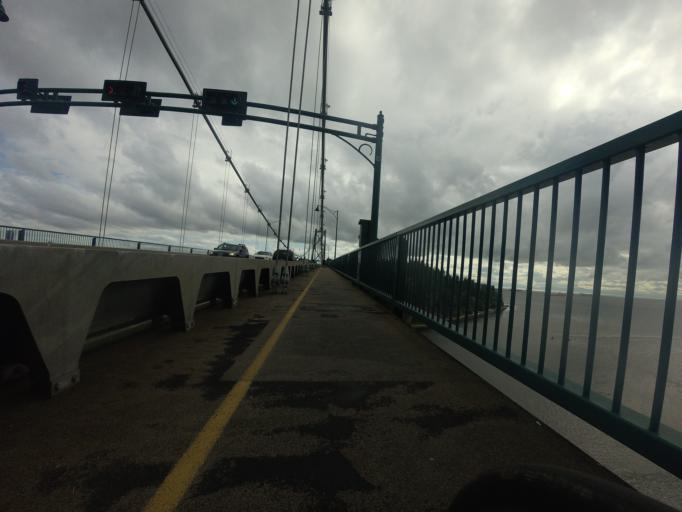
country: CA
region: British Columbia
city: West End
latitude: 49.3164
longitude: -123.1378
